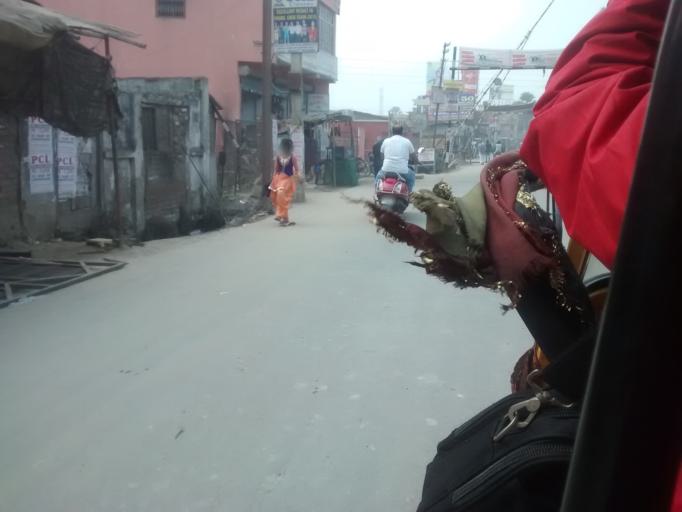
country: IN
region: Bihar
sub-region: Muzaffarpur
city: Muzaffarpur
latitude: 26.1048
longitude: 85.3966
